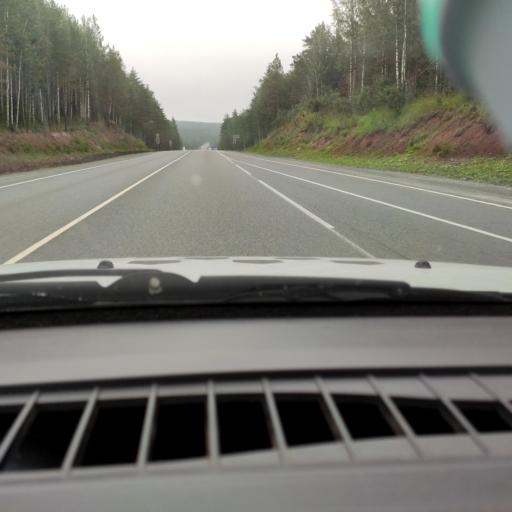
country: RU
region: Chelyabinsk
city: Zlatoust
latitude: 55.0560
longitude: 59.6868
